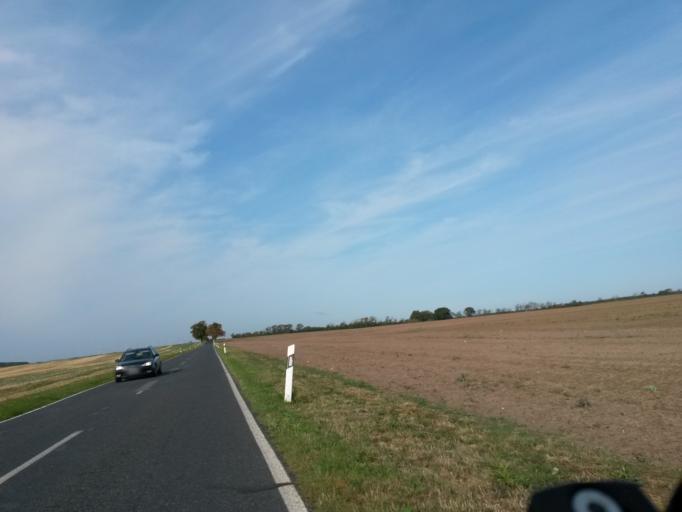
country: DE
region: Saxony-Anhalt
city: Tangermunde
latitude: 52.5405
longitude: 11.9339
